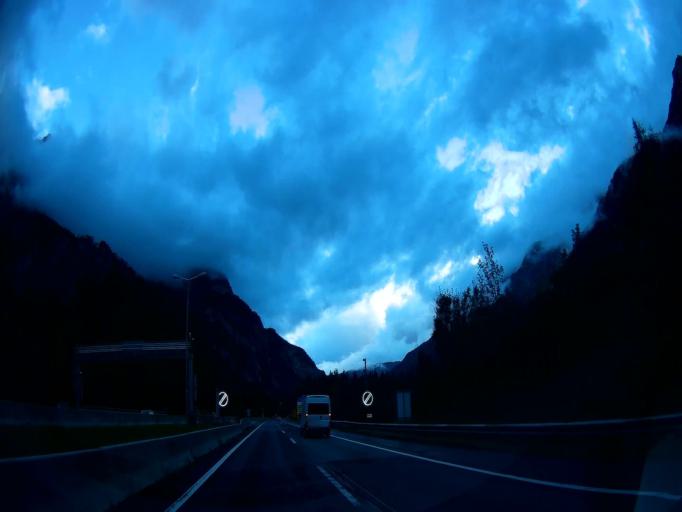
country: AT
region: Salzburg
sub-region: Politischer Bezirk Hallein
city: Golling an der Salzach
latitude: 47.5556
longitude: 13.1730
